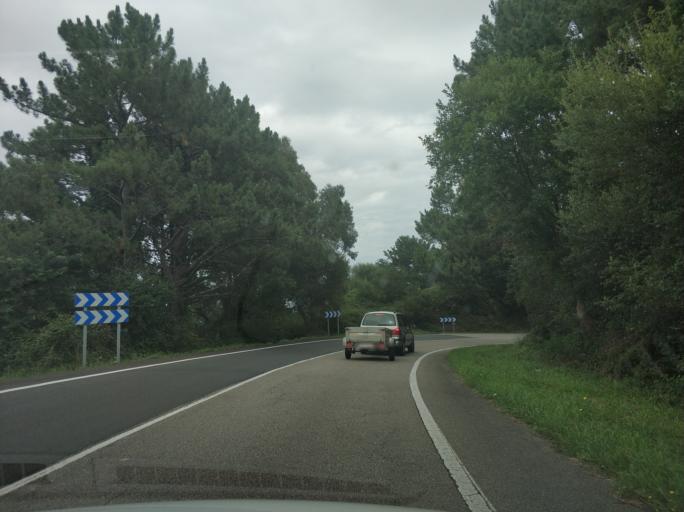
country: ES
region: Asturias
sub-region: Province of Asturias
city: Cudillero
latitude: 43.5659
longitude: -6.1559
